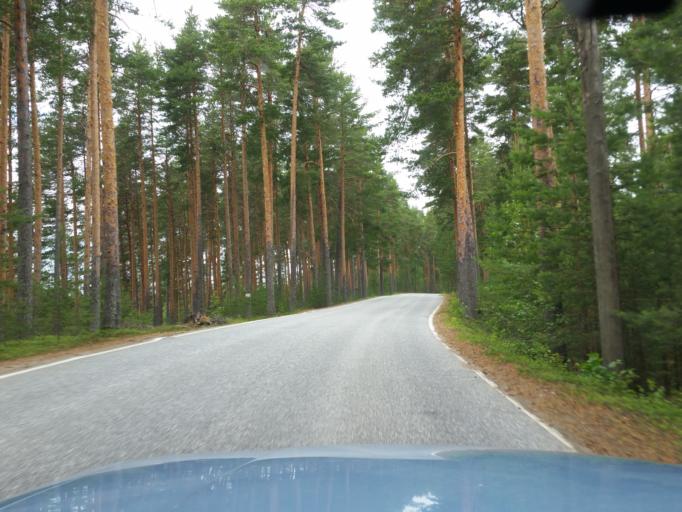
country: FI
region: Southern Savonia
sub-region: Savonlinna
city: Sulkava
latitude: 61.7747
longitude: 28.4286
